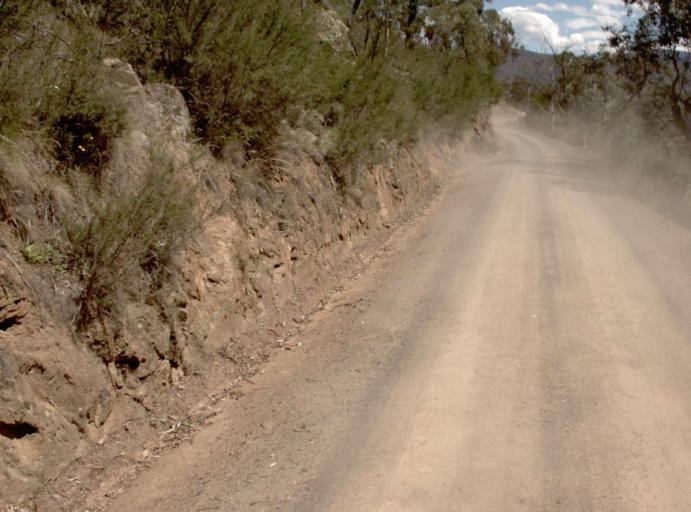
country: AU
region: New South Wales
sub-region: Snowy River
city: Jindabyne
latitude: -37.0403
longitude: 148.5384
